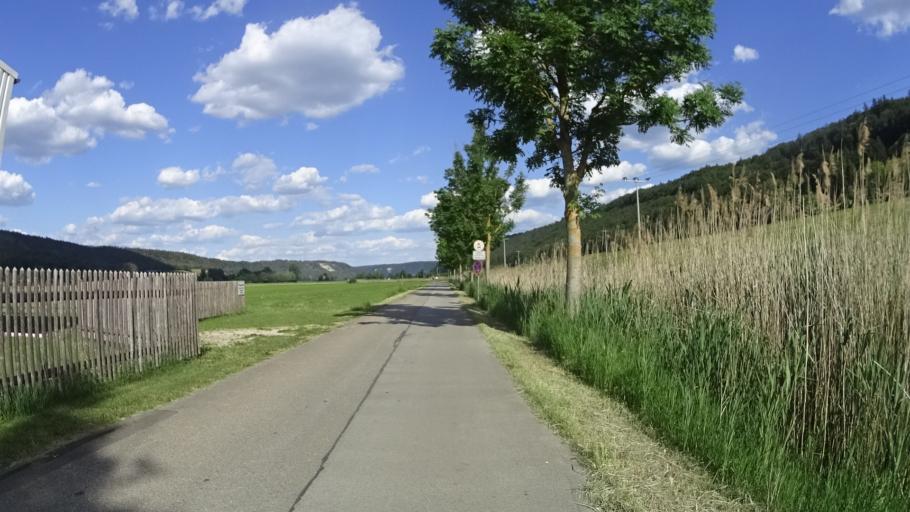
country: DE
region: Bavaria
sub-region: Upper Bavaria
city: Denkendorf
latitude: 49.0201
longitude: 11.4847
